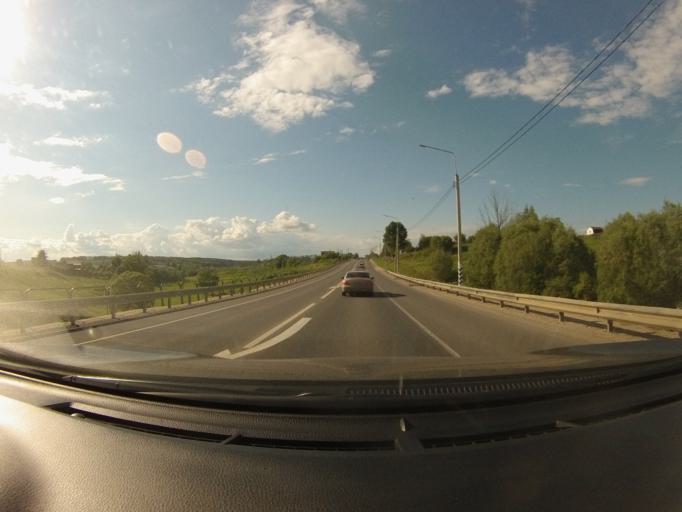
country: RU
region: Tula
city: Gorelki
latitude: 54.2977
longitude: 37.5766
